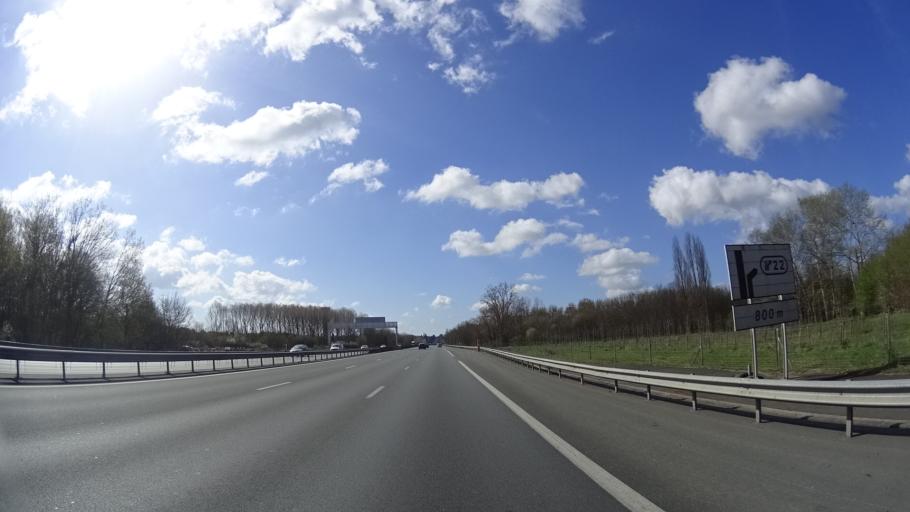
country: FR
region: Pays de la Loire
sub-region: Departement de Maine-et-Loire
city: Les Ponts-de-Ce
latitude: 47.4110
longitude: -0.5079
